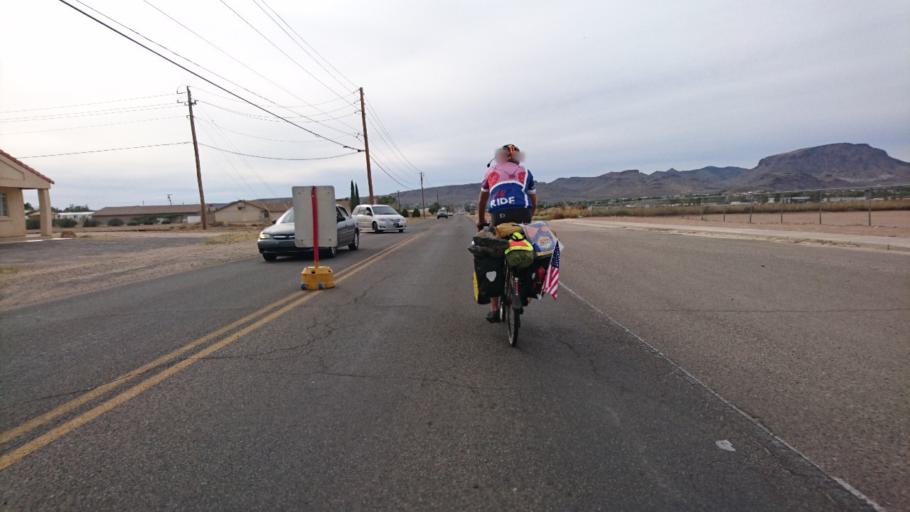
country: US
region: Arizona
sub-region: Mohave County
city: New Kingman-Butler
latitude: 35.2393
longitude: -114.0050
